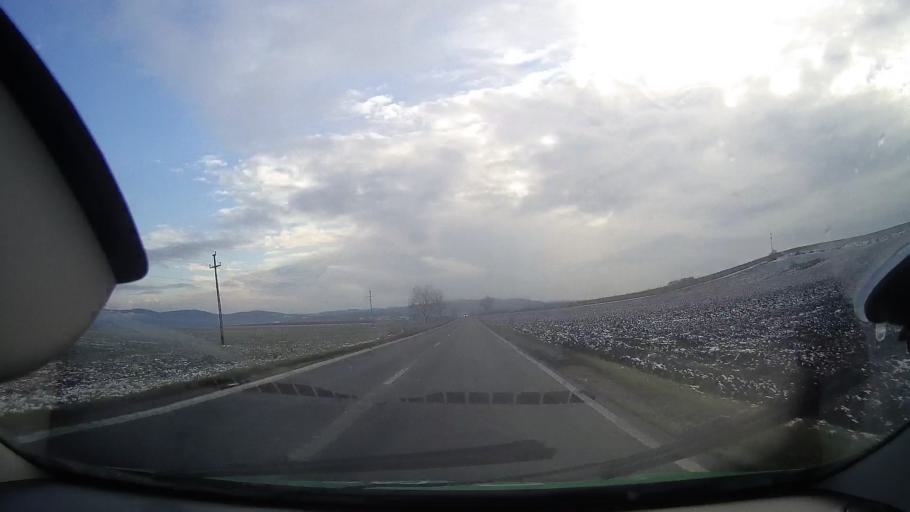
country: RO
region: Mures
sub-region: Comuna Cucerdea
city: Cucerdea
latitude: 46.4147
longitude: 24.2639
